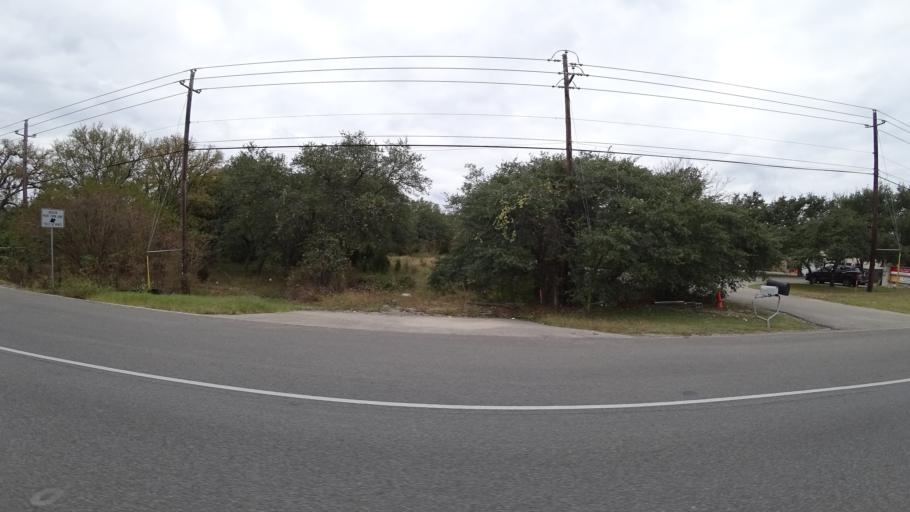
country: US
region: Texas
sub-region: Travis County
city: Bee Cave
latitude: 30.3181
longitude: -97.9505
